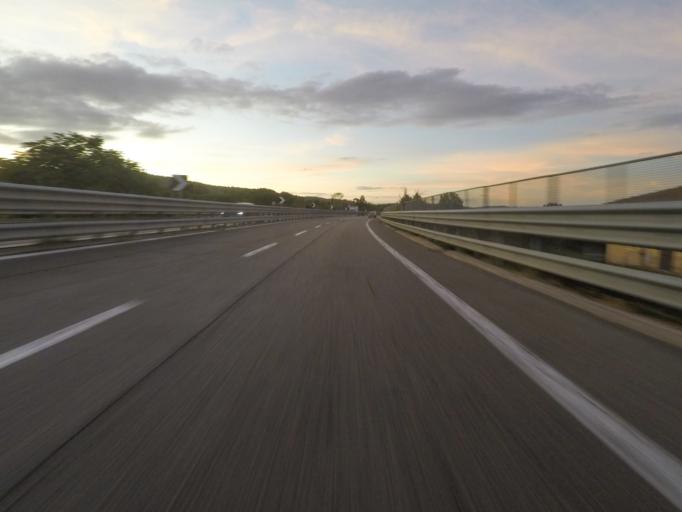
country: IT
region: Tuscany
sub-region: Provincia di Siena
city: Sinalunga
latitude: 43.2298
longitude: 11.7321
